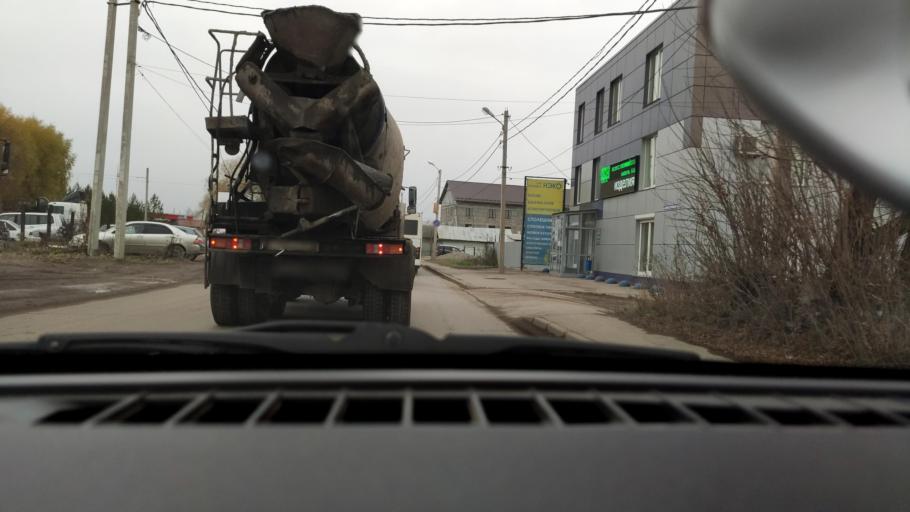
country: RU
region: Perm
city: Kondratovo
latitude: 57.9528
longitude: 56.1368
